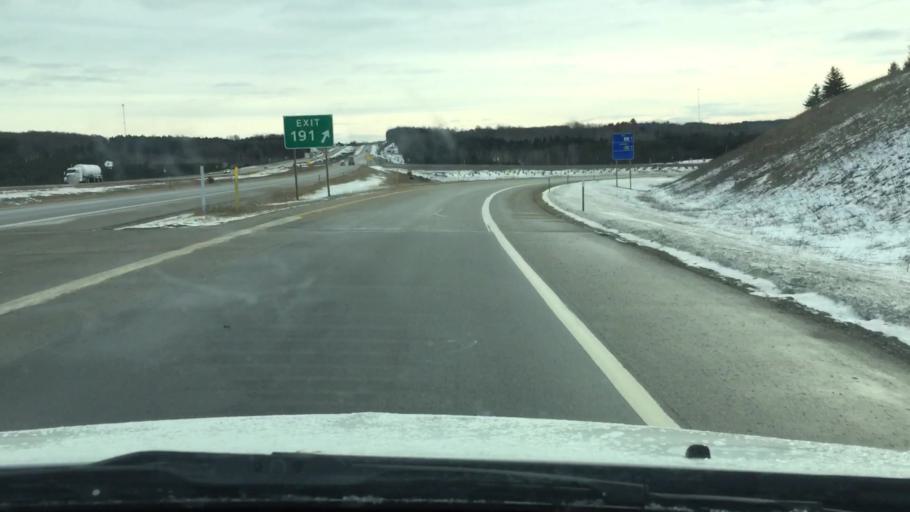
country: US
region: Michigan
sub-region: Wexford County
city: Manton
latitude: 44.4084
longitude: -85.3819
